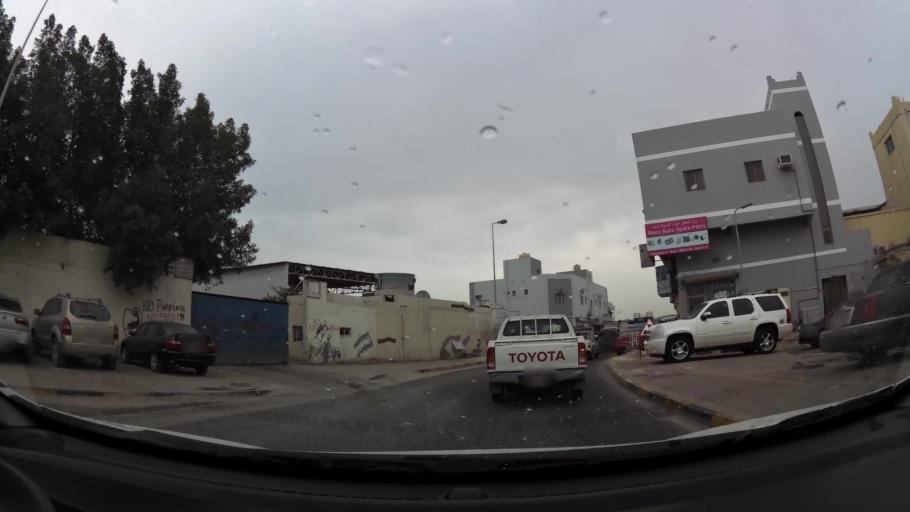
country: BH
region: Northern
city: Madinat `Isa
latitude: 26.1850
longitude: 50.5271
